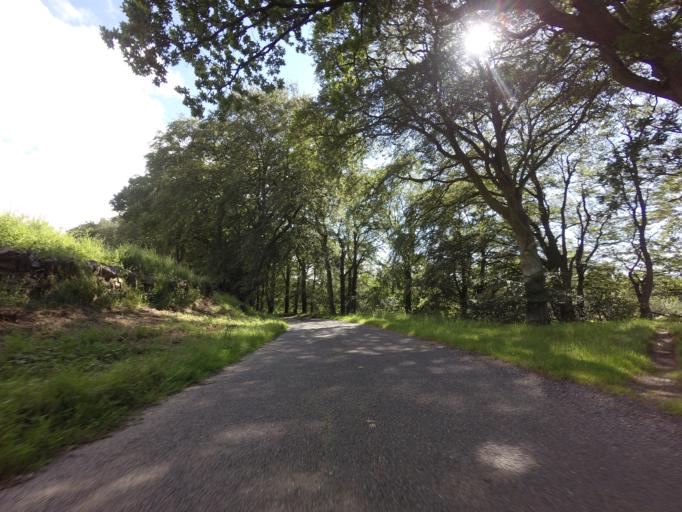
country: GB
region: Scotland
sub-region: Aberdeenshire
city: Banff
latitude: 57.6130
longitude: -2.5117
